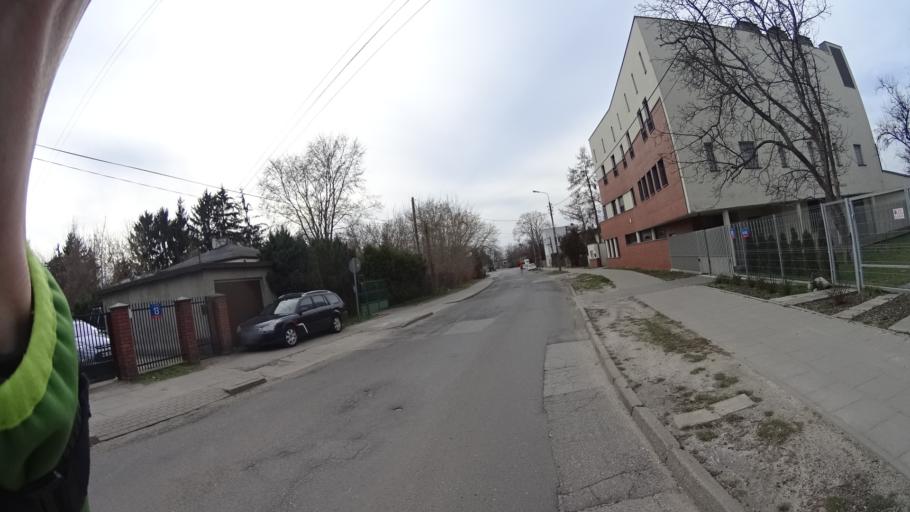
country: PL
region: Masovian Voivodeship
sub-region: Warszawa
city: Praga Poludnie
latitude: 52.2085
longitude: 21.0799
